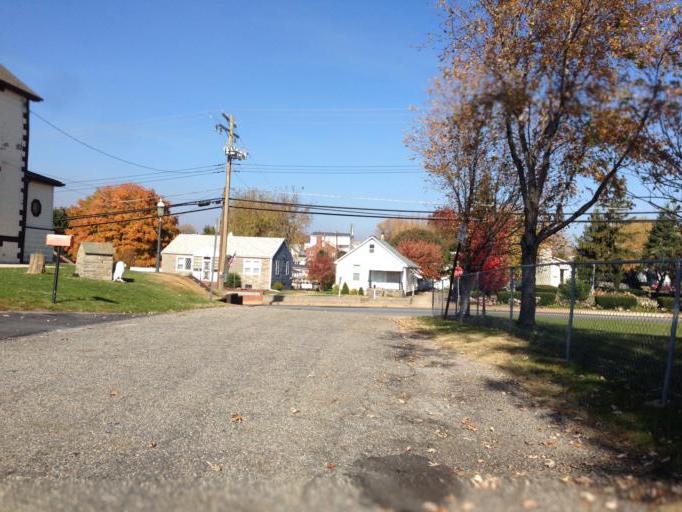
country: US
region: Maryland
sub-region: Baltimore County
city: Dundalk
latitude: 39.2823
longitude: -76.5231
